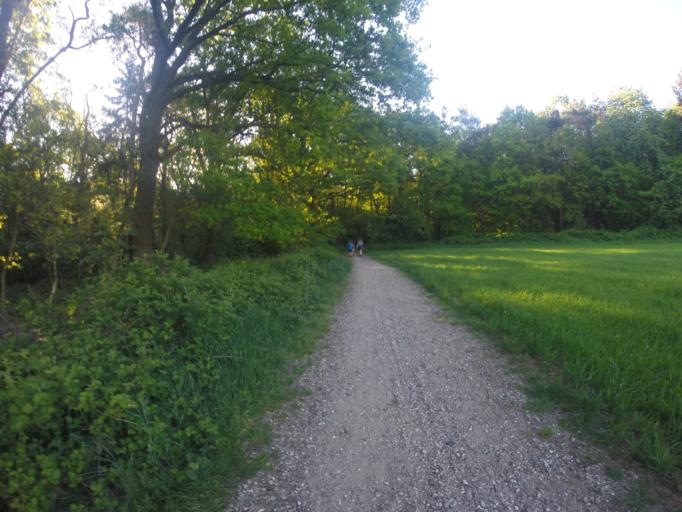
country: NL
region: Gelderland
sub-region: Gemeente Montferland
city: s-Heerenberg
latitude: 51.9086
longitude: 6.2018
